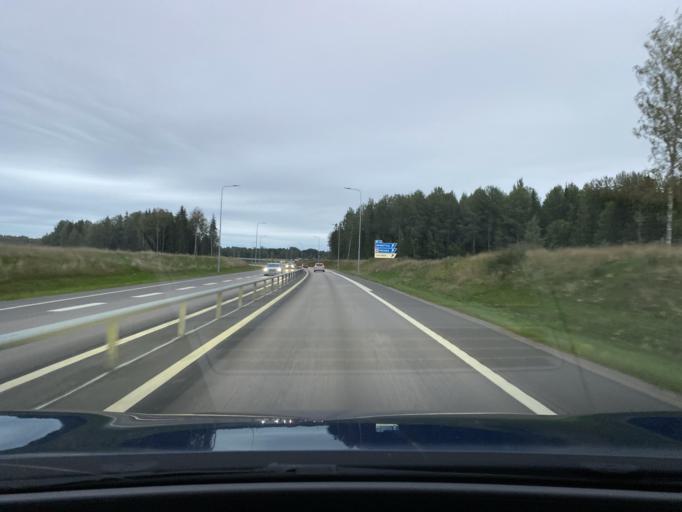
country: FI
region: Paijanne Tavastia
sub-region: Lahti
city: Lahti
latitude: 60.9526
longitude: 25.5827
